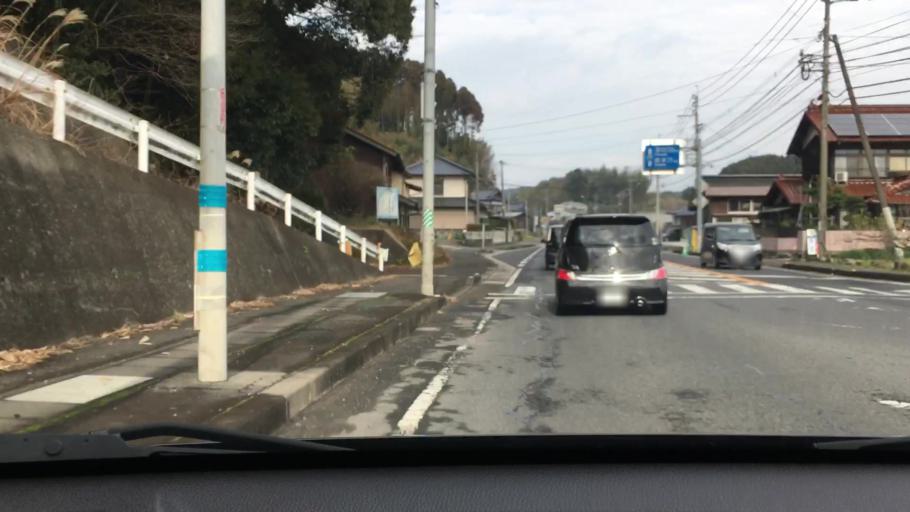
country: JP
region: Saga Prefecture
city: Imaricho-ko
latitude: 33.3068
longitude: 129.9261
